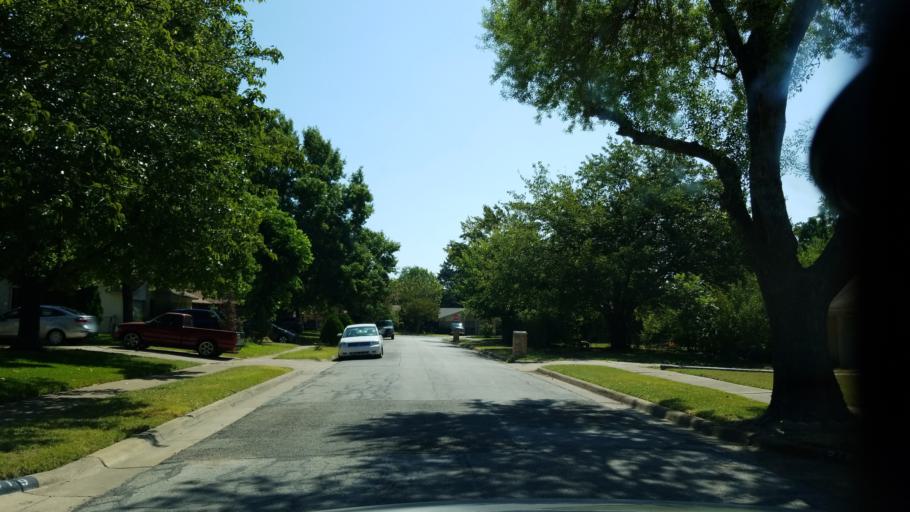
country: US
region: Texas
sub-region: Dallas County
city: Duncanville
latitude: 32.6429
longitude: -96.9000
